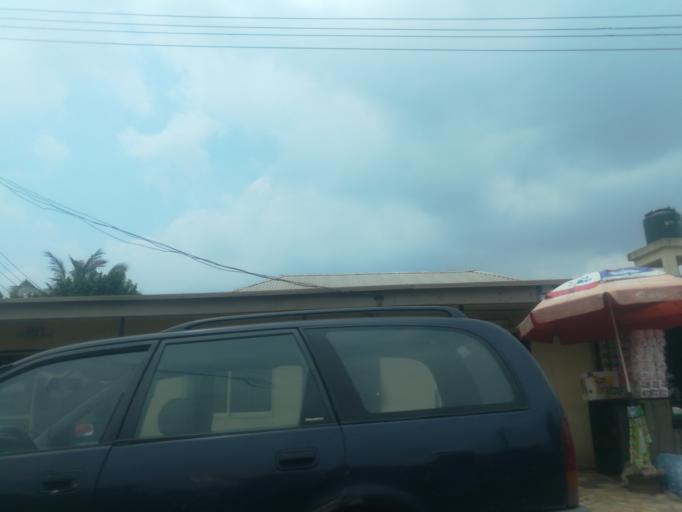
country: NG
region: Oyo
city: Ibadan
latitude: 7.4216
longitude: 3.9191
